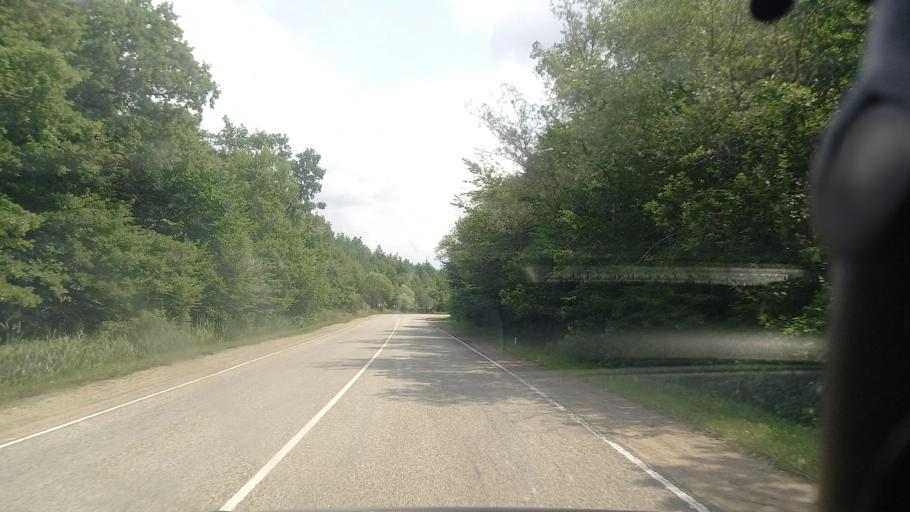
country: RU
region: Karachayevo-Cherkesiya
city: Kurdzhinovo
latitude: 44.0383
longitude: 40.9108
